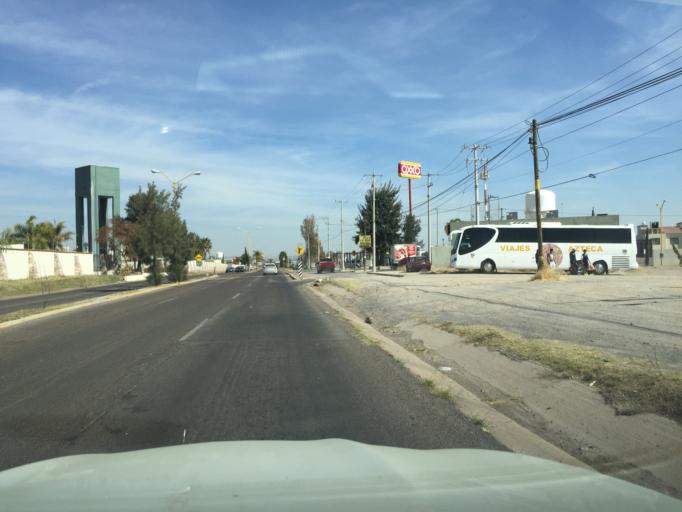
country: MX
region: Aguascalientes
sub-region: Aguascalientes
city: La Loma de los Negritos
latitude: 21.8576
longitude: -102.3465
